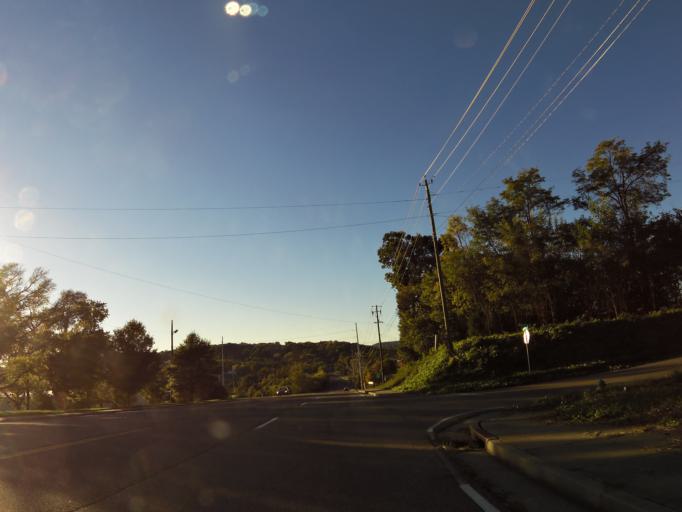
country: US
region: Tennessee
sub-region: Knox County
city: Knoxville
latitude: 35.9674
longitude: -83.9471
